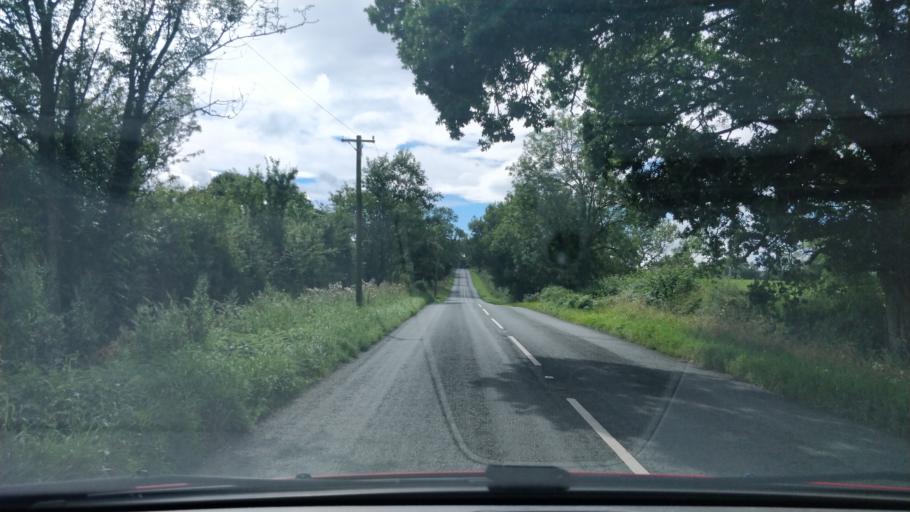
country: GB
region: Wales
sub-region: County of Flintshire
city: Hope
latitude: 53.1312
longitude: -3.0217
